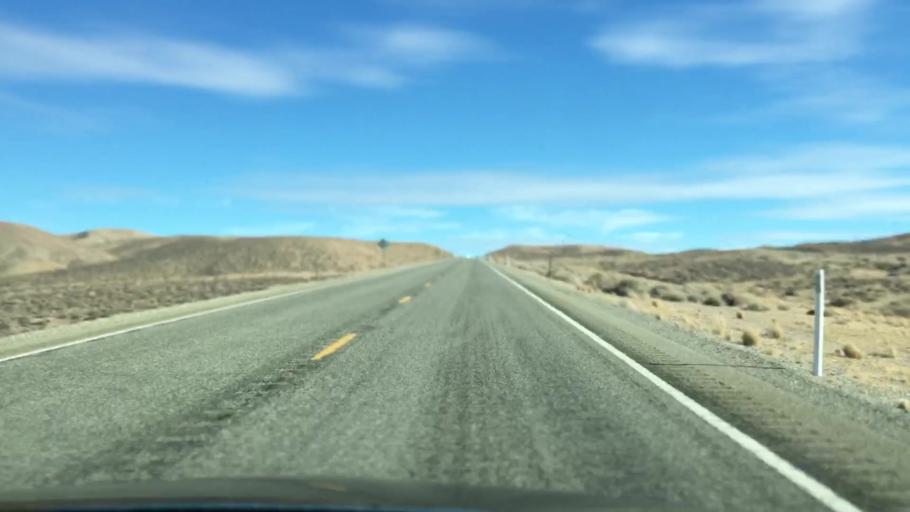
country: US
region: Nevada
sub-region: Lyon County
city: Yerington
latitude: 39.0458
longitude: -118.9660
